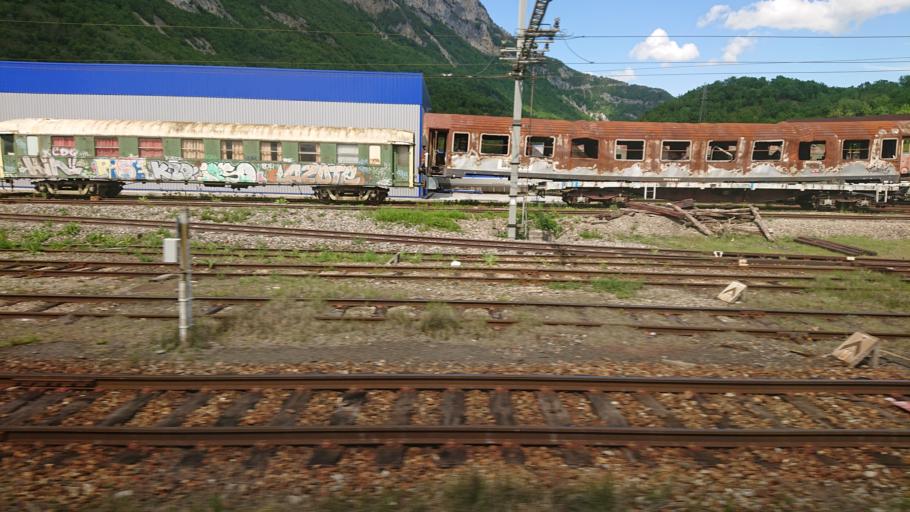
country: FR
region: Rhone-Alpes
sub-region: Departement de l'Ain
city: Culoz
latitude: 45.8452
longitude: 5.7689
